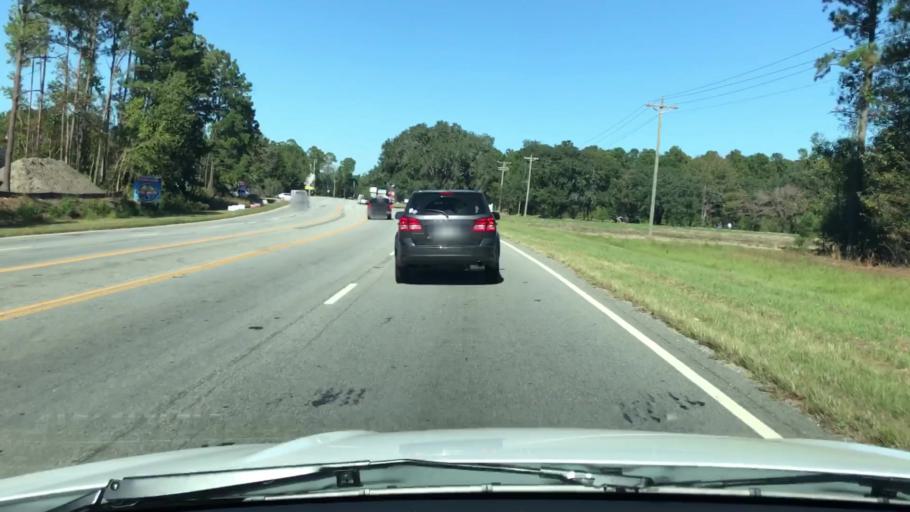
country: US
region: South Carolina
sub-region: Beaufort County
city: Bluffton
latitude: 32.3000
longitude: -80.9349
